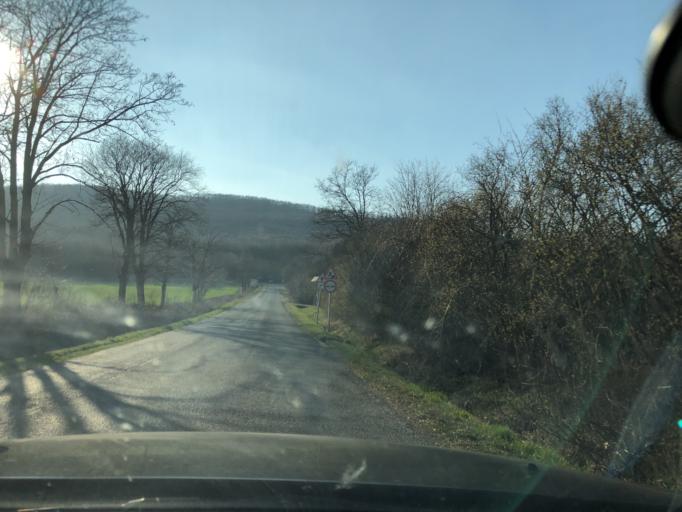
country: HU
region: Nograd
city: Paszto
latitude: 47.9329
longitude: 19.6137
